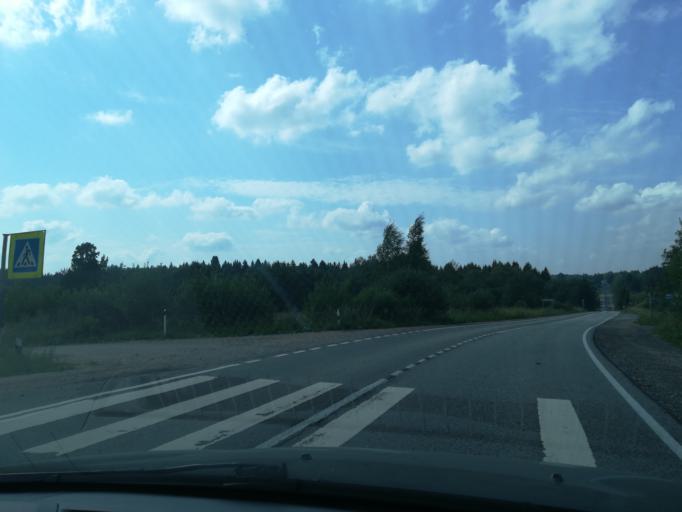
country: RU
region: Leningrad
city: Kopor'ye
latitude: 59.6380
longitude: 28.9890
